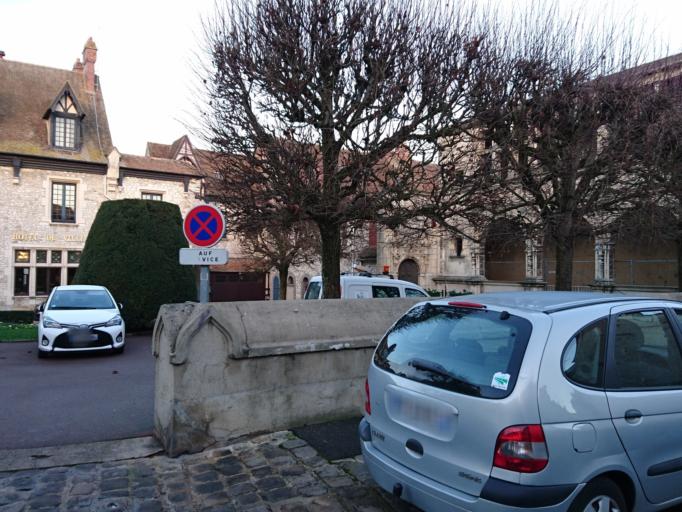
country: FR
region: Ile-de-France
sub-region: Departement de Seine-et-Marne
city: Moret-sur-Loing
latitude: 48.3728
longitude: 2.8161
